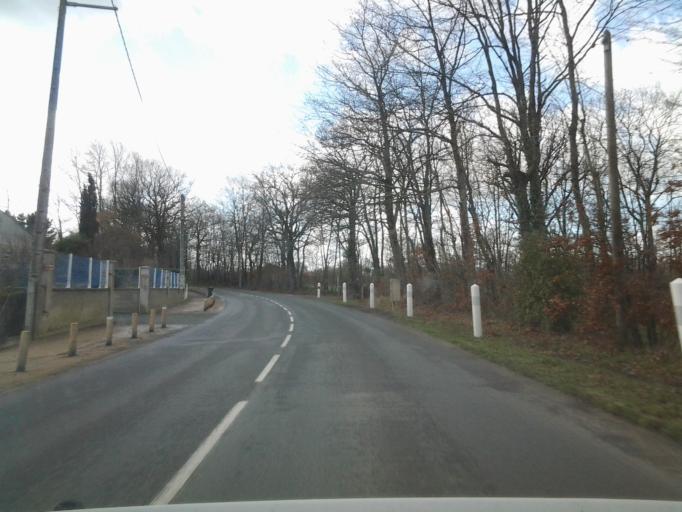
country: FR
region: Pays de la Loire
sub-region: Departement de la Vendee
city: Les Clouzeaux
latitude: 46.6383
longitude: -1.4687
